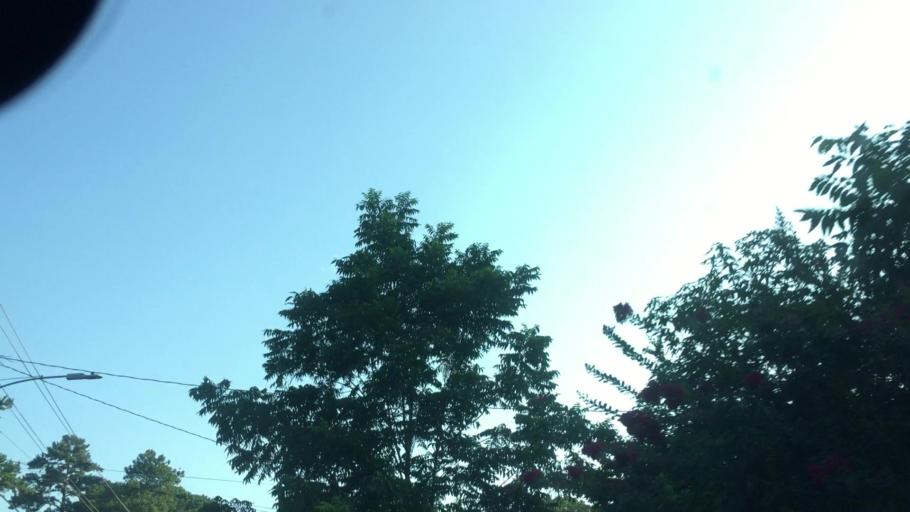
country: US
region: Georgia
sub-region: DeKalb County
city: Panthersville
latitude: 33.7062
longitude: -84.2144
